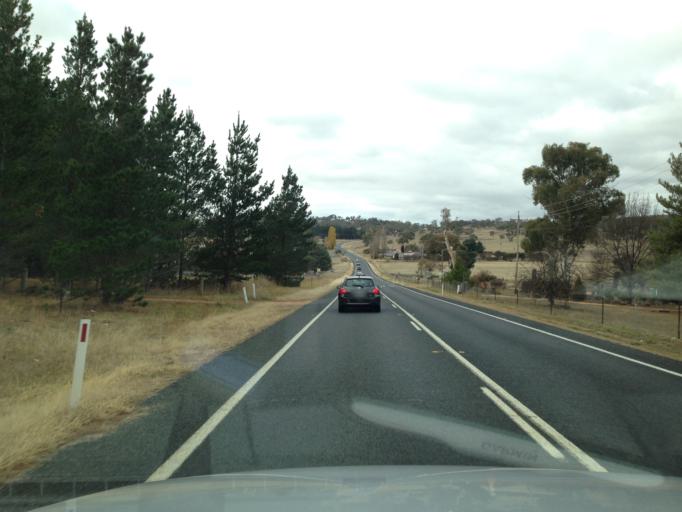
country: AU
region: New South Wales
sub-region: Cooma-Monaro
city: Cooma
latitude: -36.2445
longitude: 149.0575
